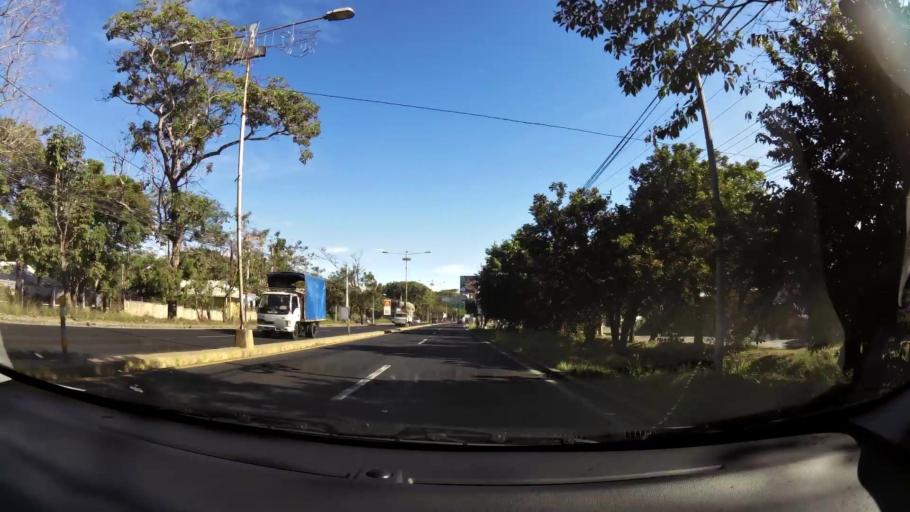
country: SV
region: Santa Ana
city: Santa Ana
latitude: 13.9737
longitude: -89.5627
